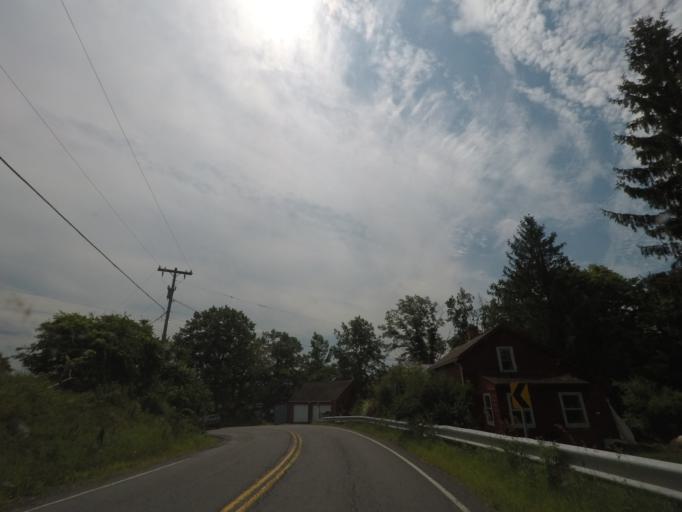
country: US
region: New York
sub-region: Rensselaer County
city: Wynantskill
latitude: 42.7353
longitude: -73.6062
